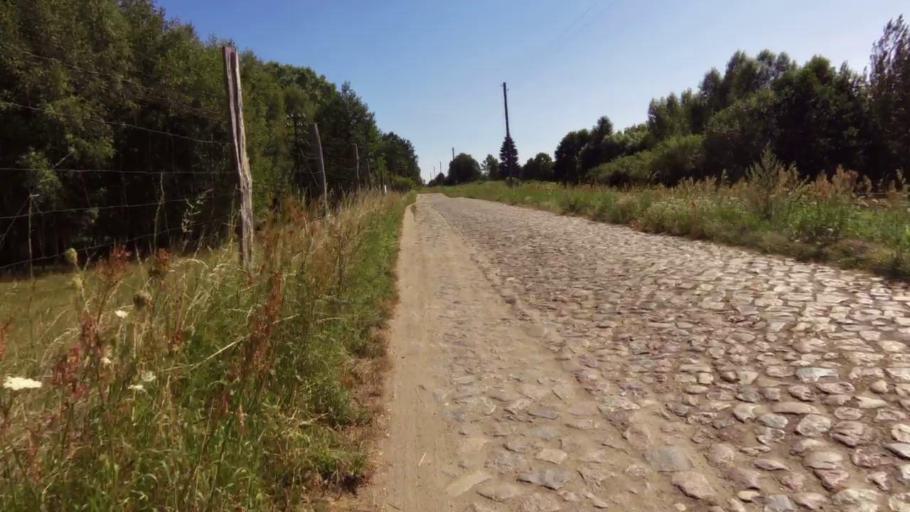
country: PL
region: West Pomeranian Voivodeship
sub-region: Powiat drawski
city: Wierzchowo
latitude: 53.5246
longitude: 16.1467
